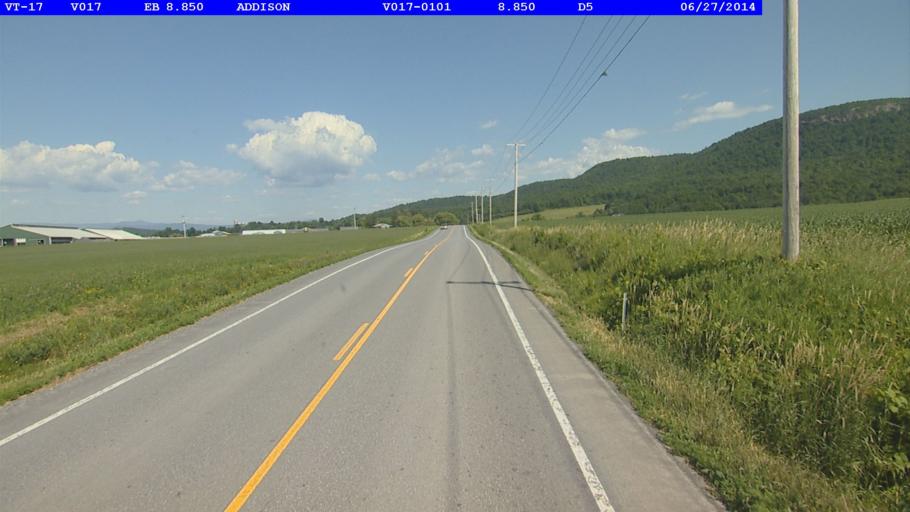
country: US
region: Vermont
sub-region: Addison County
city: Vergennes
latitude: 44.0865
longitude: -73.2935
